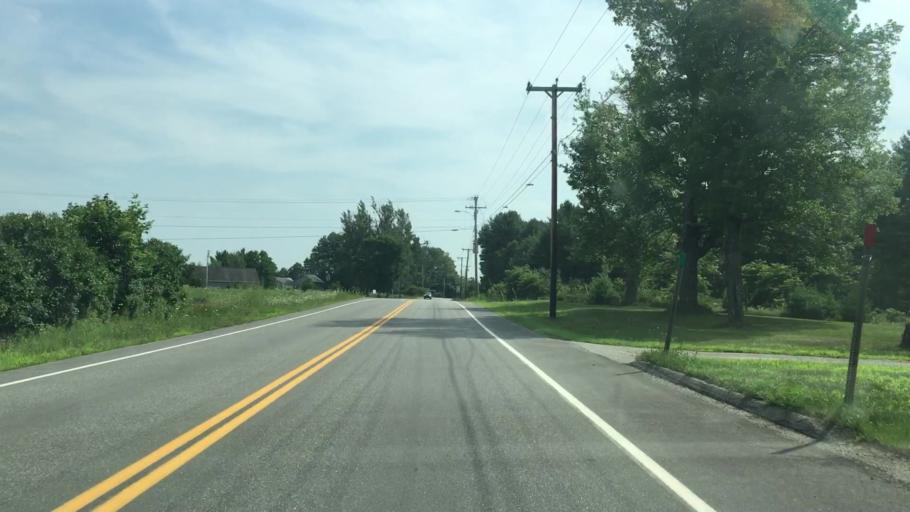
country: US
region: Maine
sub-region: Kennebec County
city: Windsor
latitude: 44.2954
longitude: -69.5852
